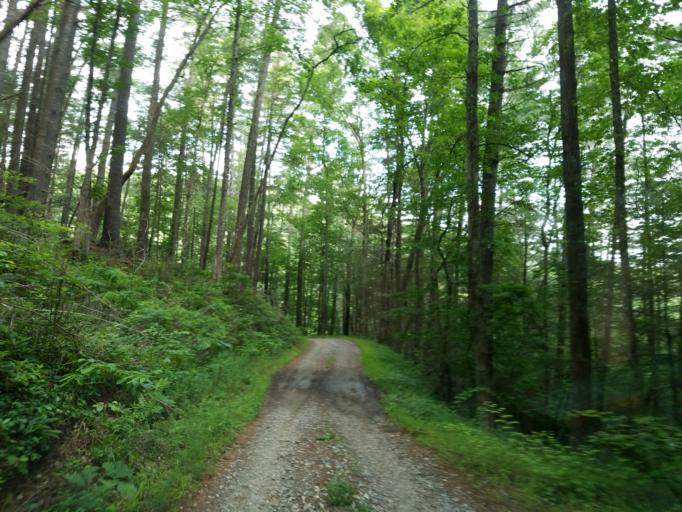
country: US
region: Georgia
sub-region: Union County
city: Blairsville
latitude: 34.7581
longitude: -84.0349
